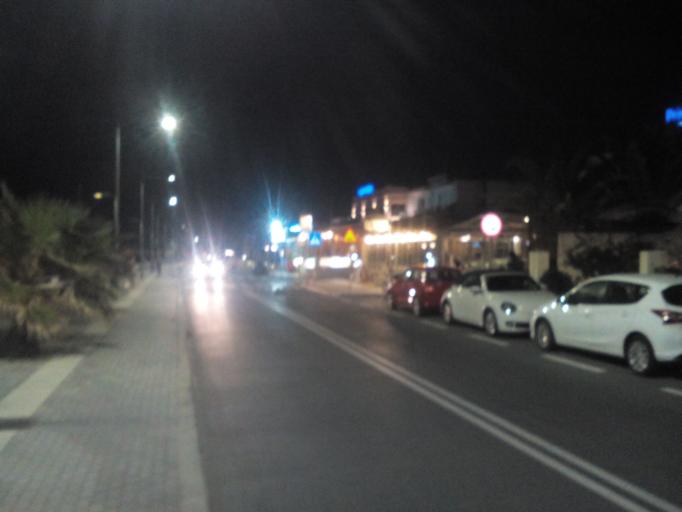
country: GR
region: Crete
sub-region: Nomos Rethymnis
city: Rethymno
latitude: 35.3682
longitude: 24.5036
